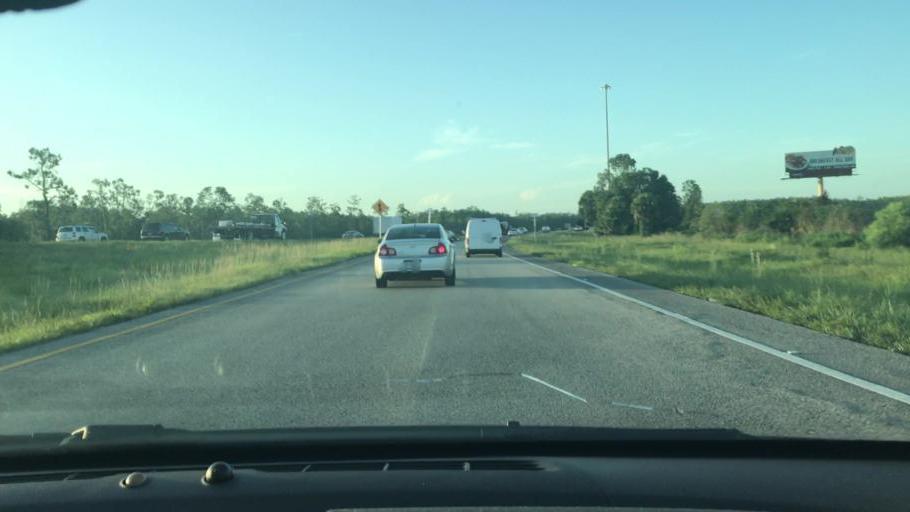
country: US
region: Florida
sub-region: Lee County
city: Fort Myers
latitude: 26.6103
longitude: -81.8035
